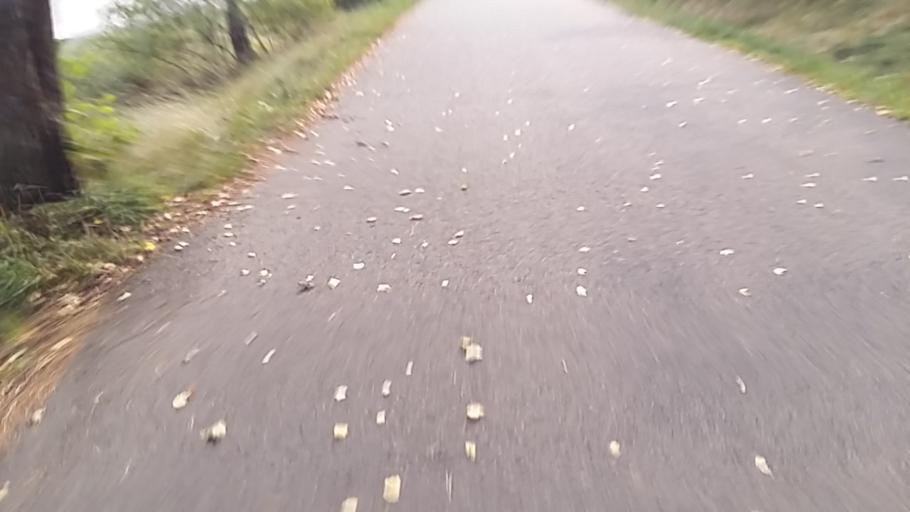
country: SE
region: Joenkoeping
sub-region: Jonkopings Kommun
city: Odensjo
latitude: 57.7419
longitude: 14.1568
